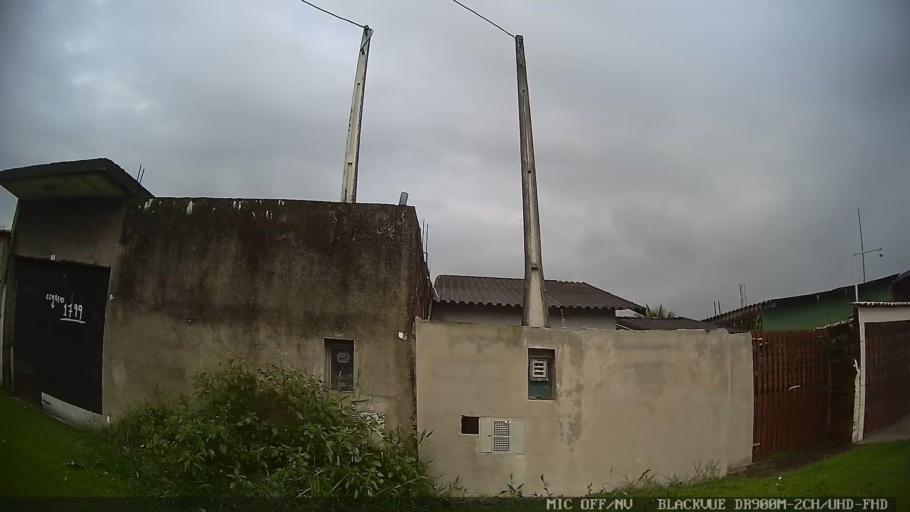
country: BR
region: Sao Paulo
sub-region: Itanhaem
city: Itanhaem
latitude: -24.1632
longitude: -46.7780
